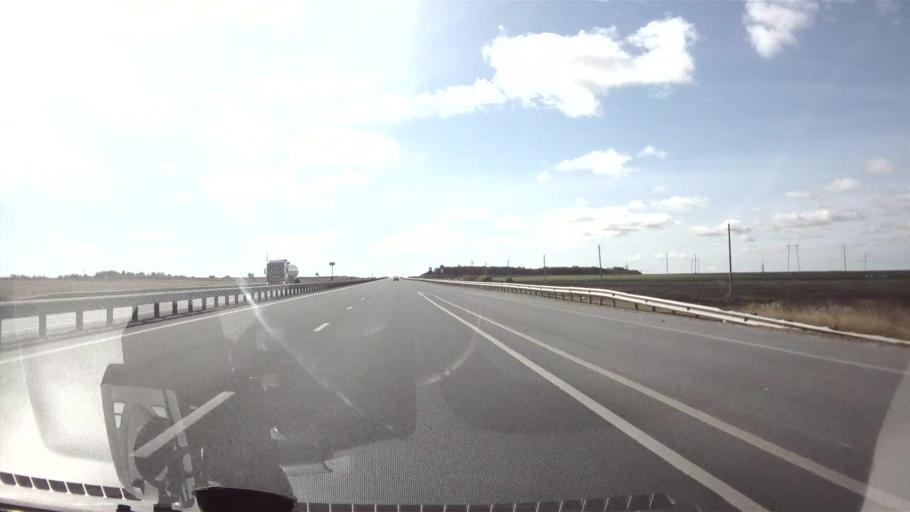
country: RU
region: Ulyanovsk
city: Novoul'yanovsk
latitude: 54.1612
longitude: 48.2645
